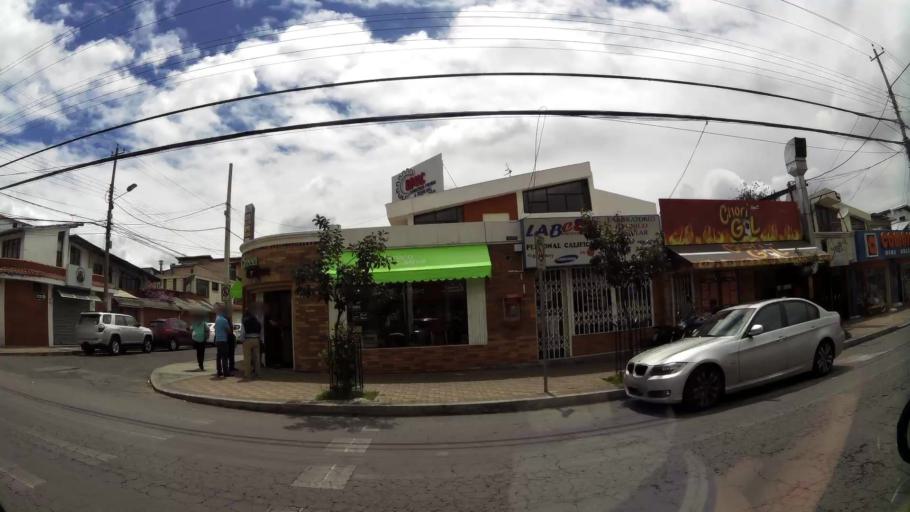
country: EC
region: Pichincha
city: Quito
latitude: -0.1649
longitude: -78.4808
